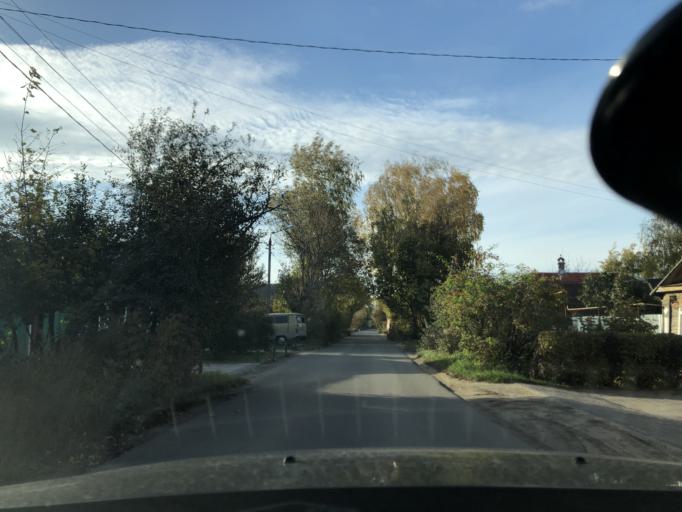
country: RU
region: Tula
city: Tula
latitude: 54.1876
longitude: 37.6368
